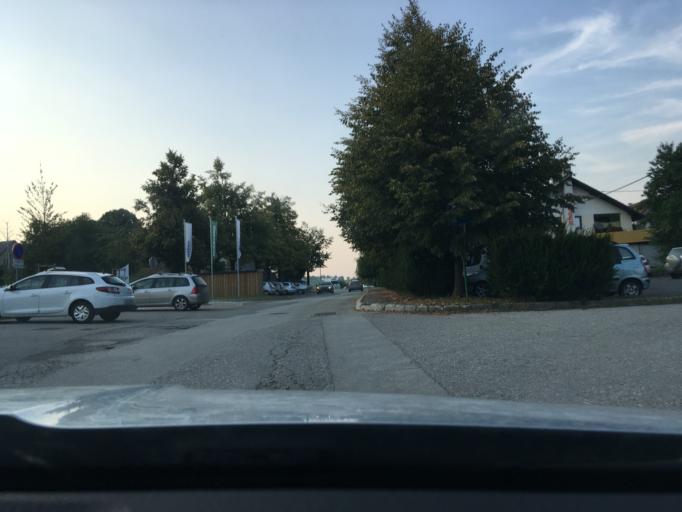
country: SI
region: Kocevje
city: Kocevje
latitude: 45.6438
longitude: 14.8714
